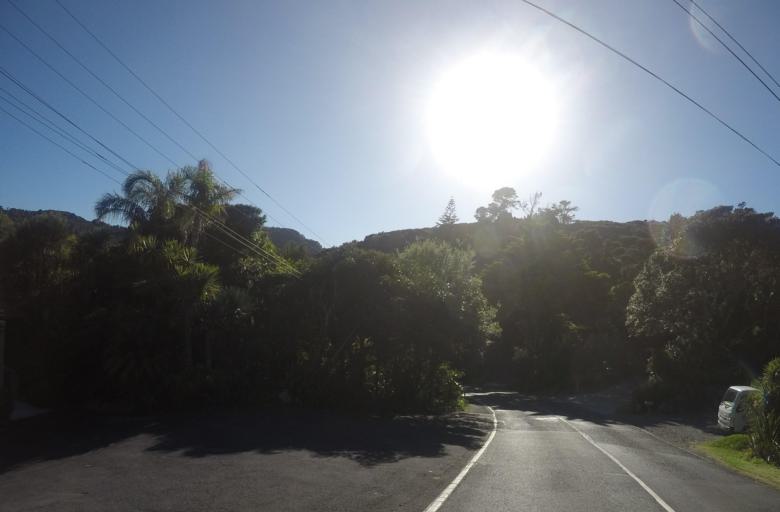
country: NZ
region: Auckland
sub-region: Auckland
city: Muriwai Beach
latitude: -36.9564
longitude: 174.4739
